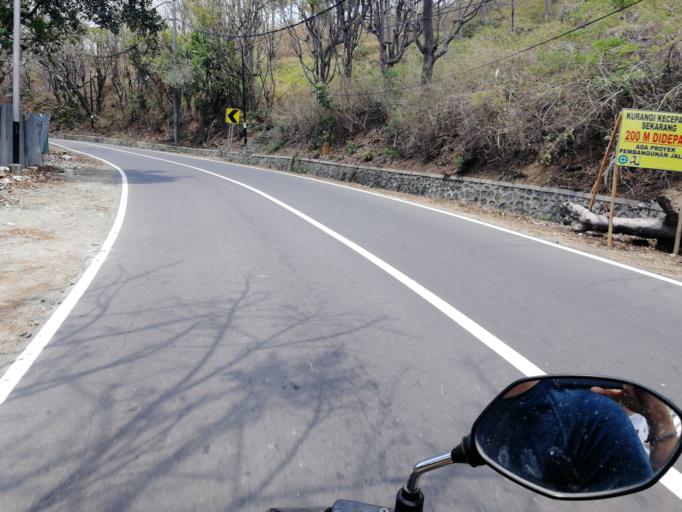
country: ID
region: West Nusa Tenggara
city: Karangsubagan
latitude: -8.4458
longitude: 116.0345
